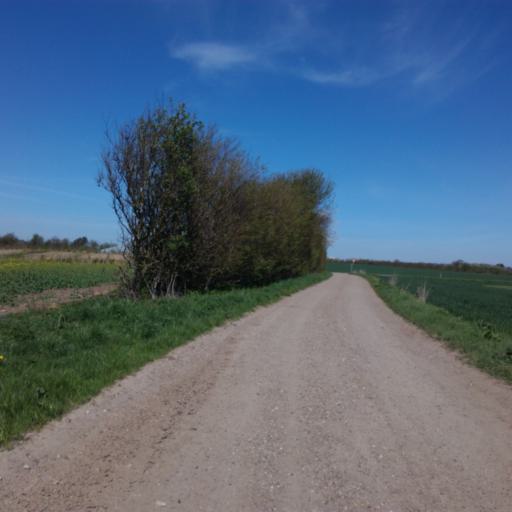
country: DK
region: South Denmark
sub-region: Vejle Kommune
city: Borkop
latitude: 55.6167
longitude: 9.6810
